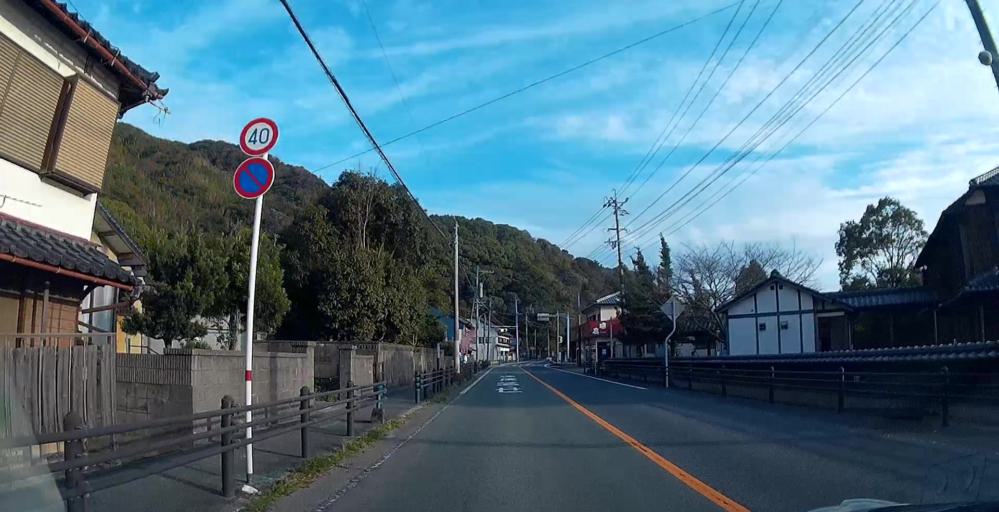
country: JP
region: Nagasaki
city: Shimabara
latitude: 32.6231
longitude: 130.4556
